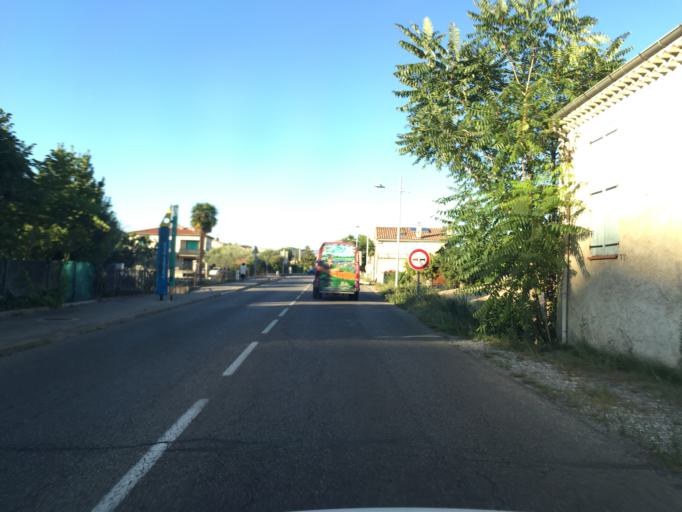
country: FR
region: Provence-Alpes-Cote d'Azur
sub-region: Departement des Alpes-de-Haute-Provence
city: Peyruis
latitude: 44.0298
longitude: 5.9419
